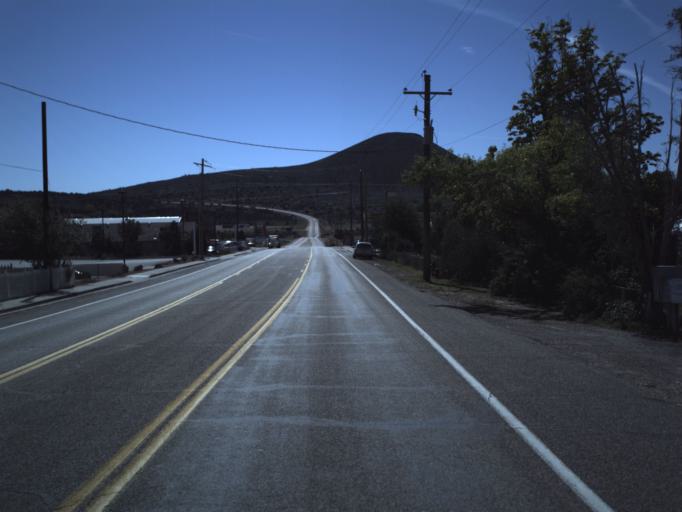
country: US
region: Utah
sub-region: Washington County
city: Ivins
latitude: 37.3396
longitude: -113.6933
